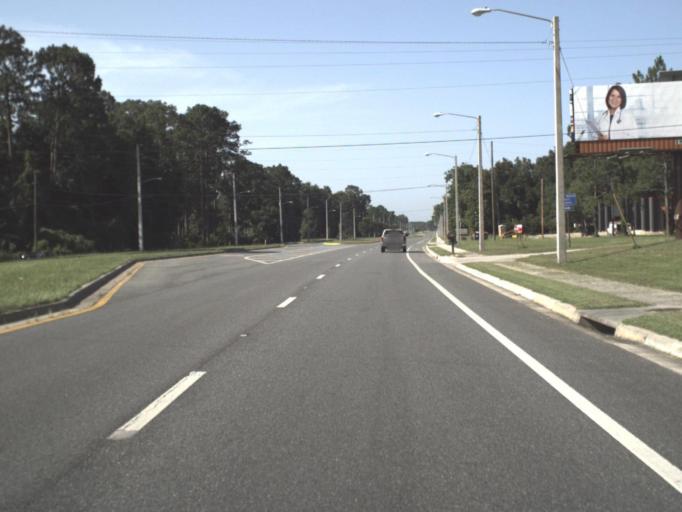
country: US
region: Florida
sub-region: Columbia County
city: Lake City
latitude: 30.1397
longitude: -82.6507
